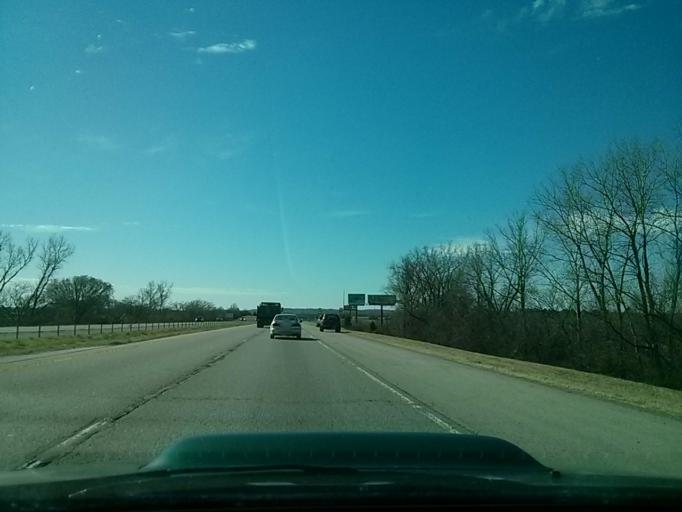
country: US
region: Oklahoma
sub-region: Tulsa County
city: Jenks
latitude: 36.0397
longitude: -96.0069
